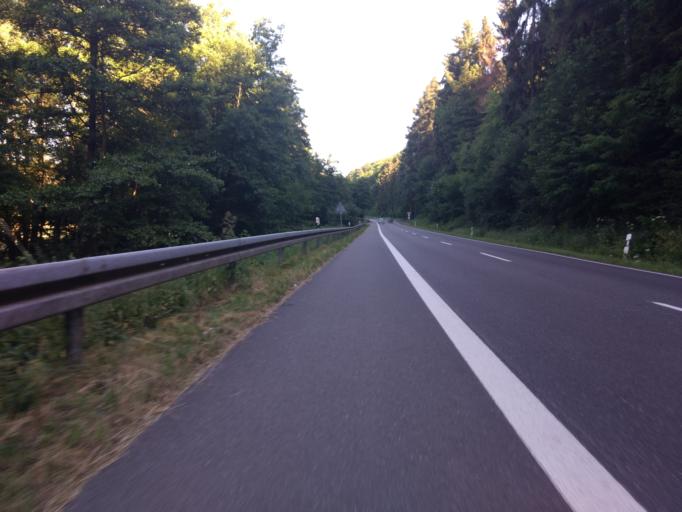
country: DE
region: Saarland
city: Merzig
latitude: 49.4357
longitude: 6.6219
